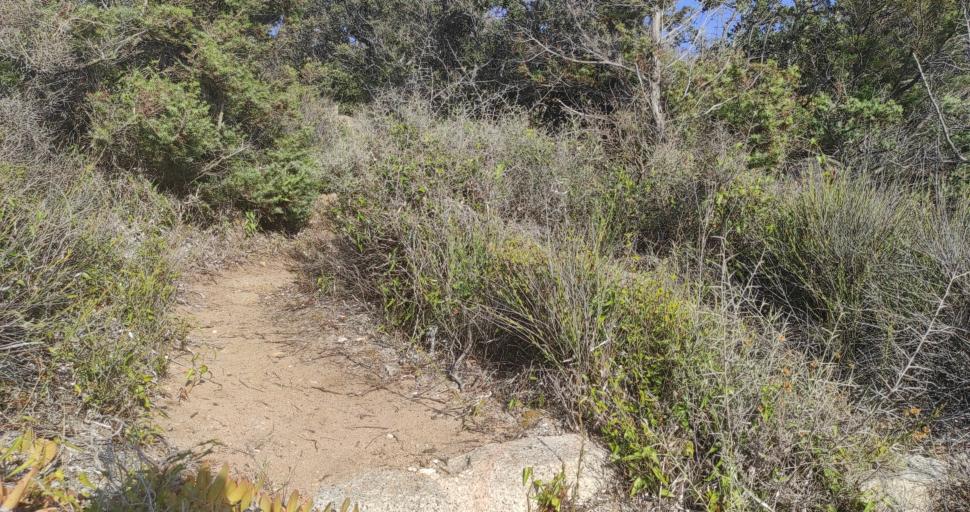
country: FR
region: Corsica
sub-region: Departement de la Corse-du-Sud
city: Porto-Vecchio
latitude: 41.6176
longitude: 9.3531
